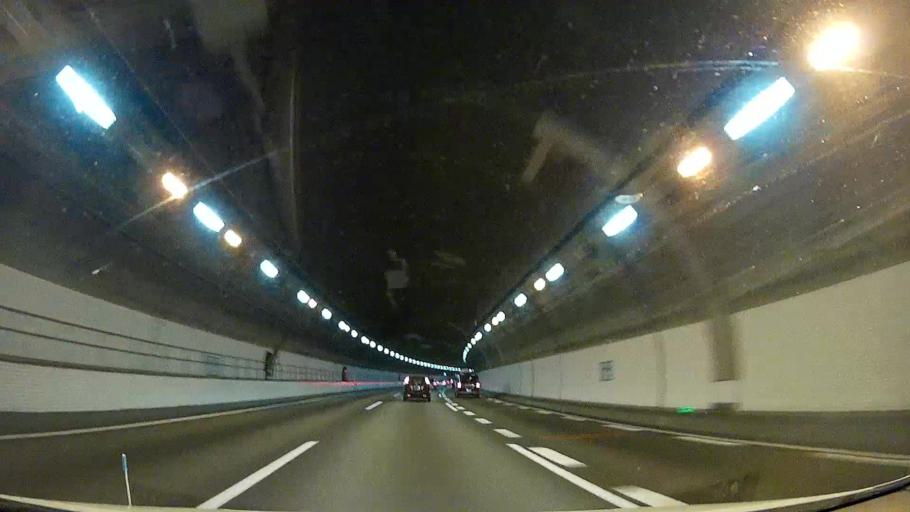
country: JP
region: Shizuoka
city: Gotemba
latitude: 35.3612
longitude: 139.0252
